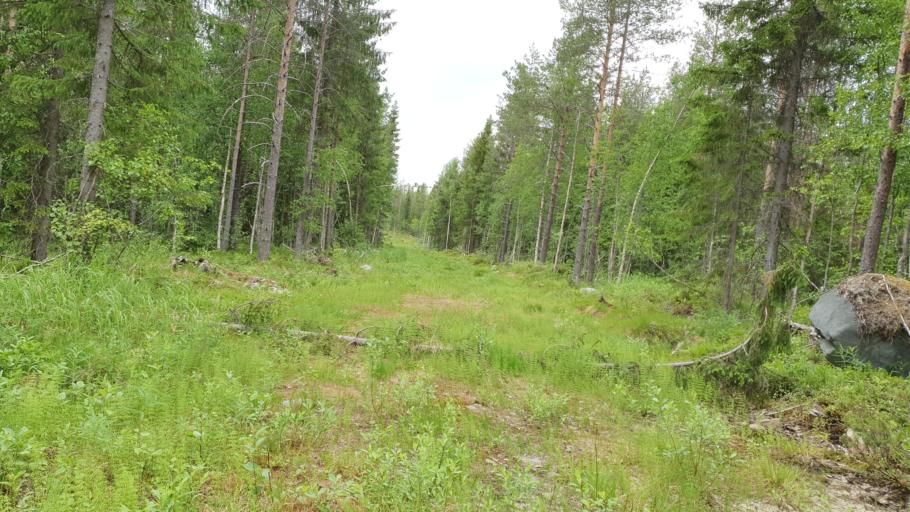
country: FI
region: Kainuu
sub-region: Kehys-Kainuu
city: Kuhmo
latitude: 64.4422
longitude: 29.6893
